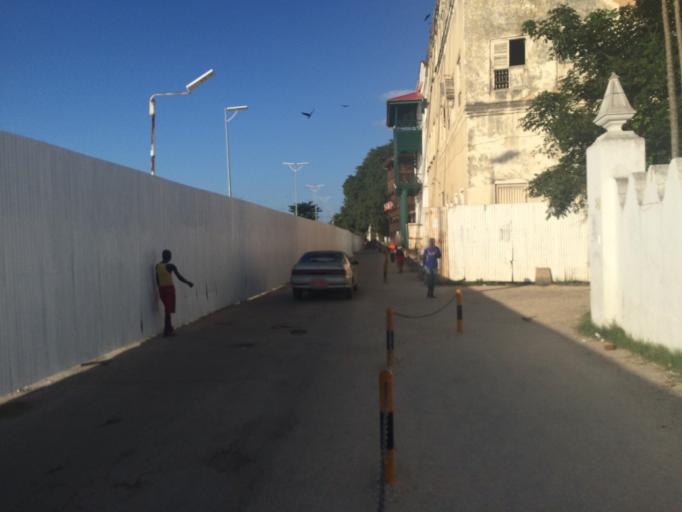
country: TZ
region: Zanzibar Urban/West
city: Zanzibar
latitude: -6.1595
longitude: 39.1908
